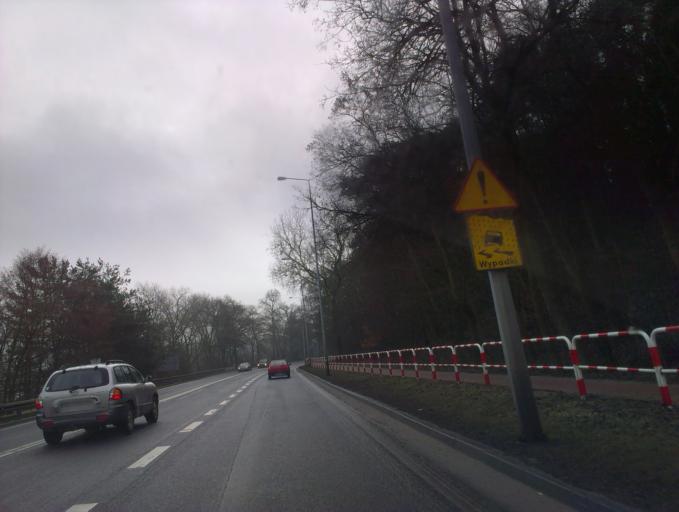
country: PL
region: Greater Poland Voivodeship
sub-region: Powiat chodzieski
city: Chodziez
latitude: 52.9839
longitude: 16.9245
